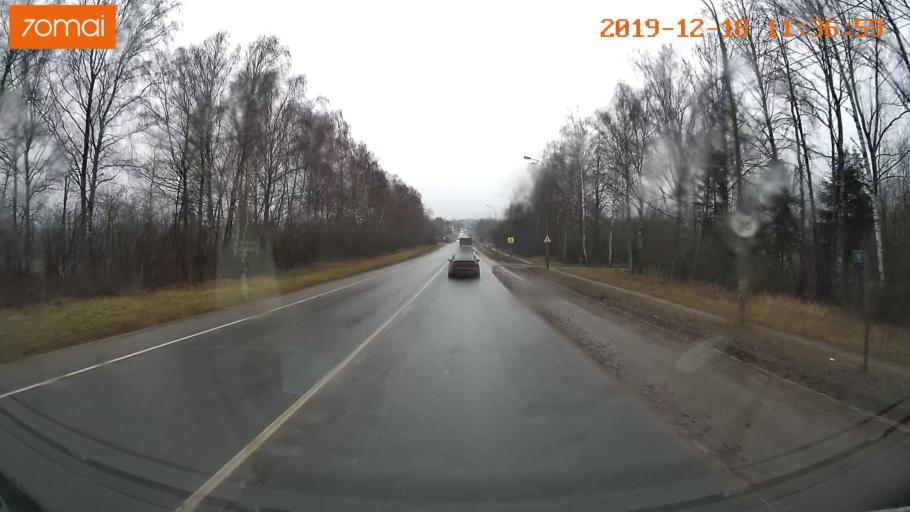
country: RU
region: Moskovskaya
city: Zvenigorod
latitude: 55.6867
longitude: 36.8994
